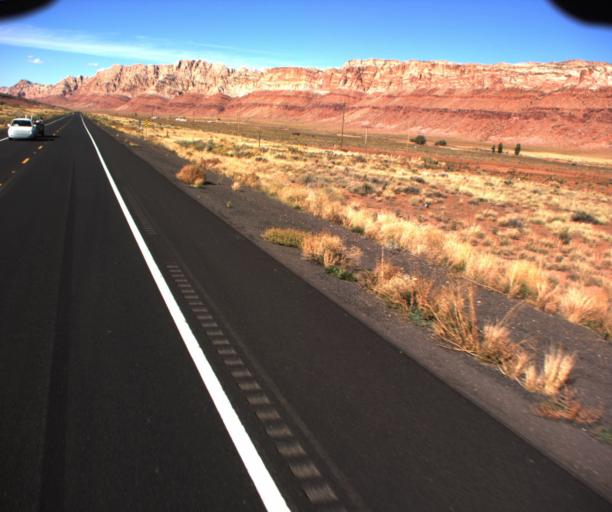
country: US
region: Arizona
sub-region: Coconino County
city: LeChee
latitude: 36.4761
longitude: -111.5721
